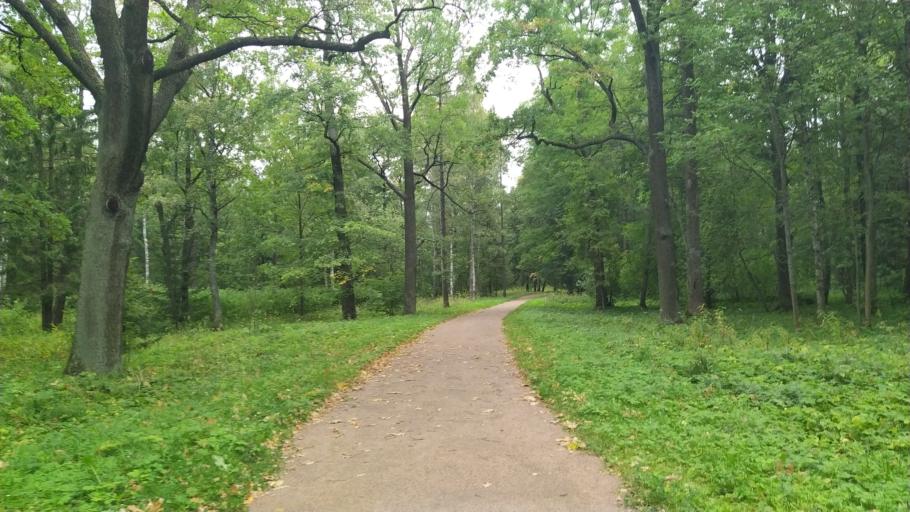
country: RU
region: St.-Petersburg
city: Pushkin
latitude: 59.7214
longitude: 30.3842
